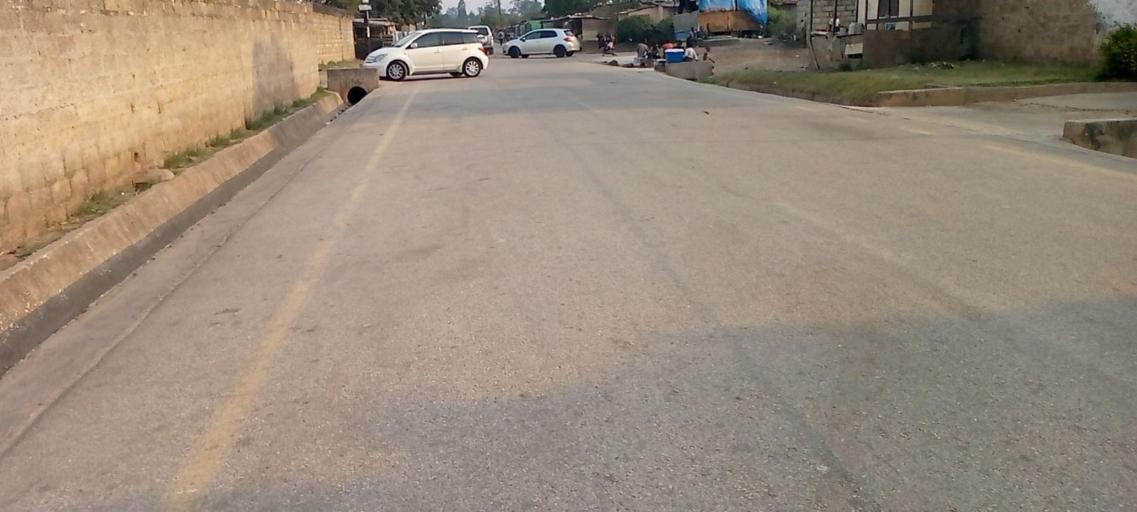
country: ZM
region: Lusaka
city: Lusaka
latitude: -15.4032
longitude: 28.3447
